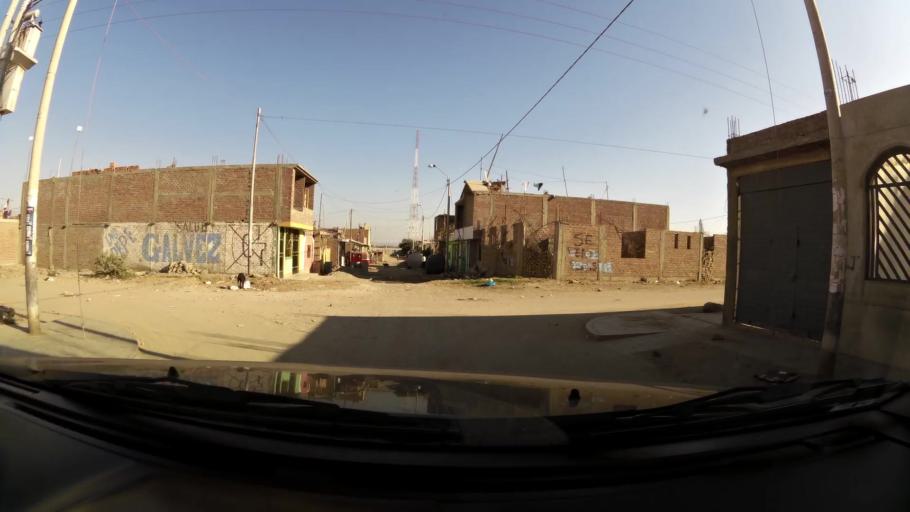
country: PE
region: Ica
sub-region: Provincia de Ica
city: La Tinguina
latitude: -14.0536
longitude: -75.6943
